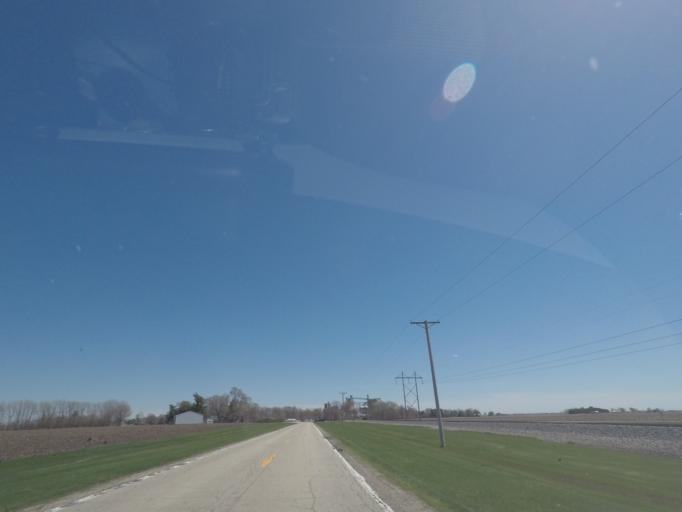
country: US
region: Illinois
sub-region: Macon County
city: Warrensburg
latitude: 39.9693
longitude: -89.1719
